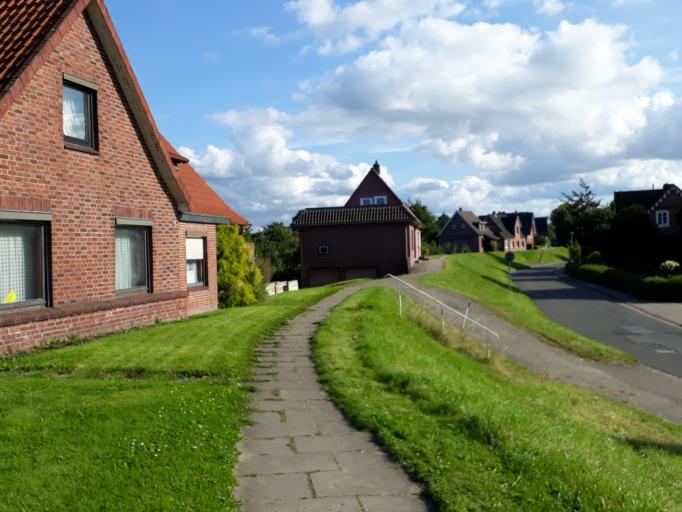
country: DE
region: Lower Saxony
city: Jork
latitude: 53.5167
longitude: 9.7259
